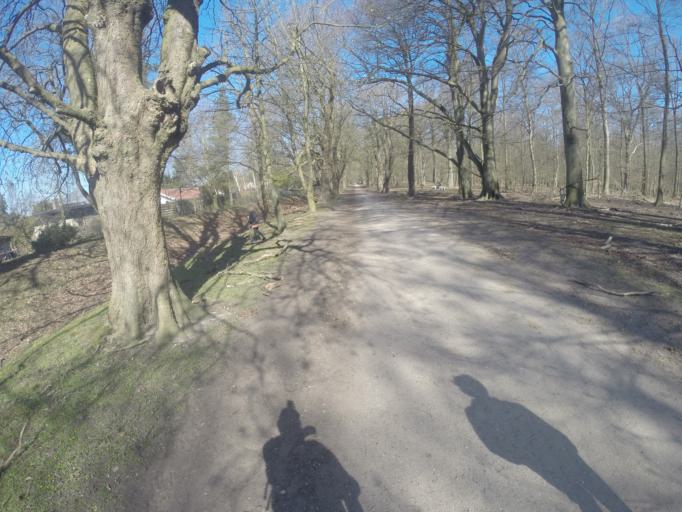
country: DK
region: Capital Region
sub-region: Lyngby-Tarbaek Kommune
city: Kongens Lyngby
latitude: 55.7796
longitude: 12.5446
